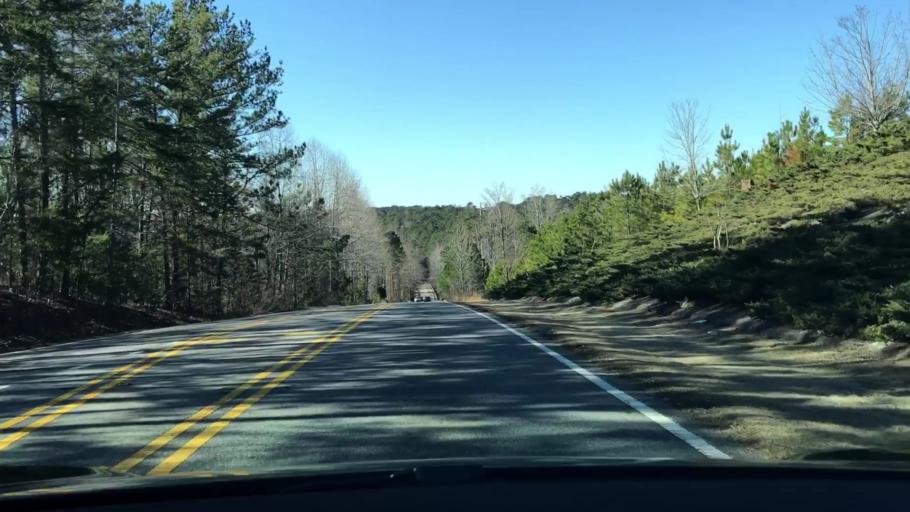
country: US
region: Georgia
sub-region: Forsyth County
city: Cumming
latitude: 34.1852
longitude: -84.1088
